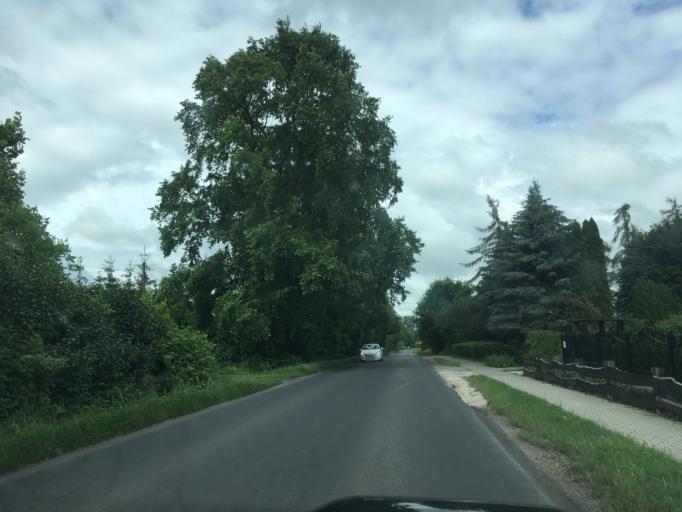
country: PL
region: Lublin Voivodeship
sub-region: Powiat swidnicki
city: Melgiew
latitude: 51.2162
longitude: 22.7518
